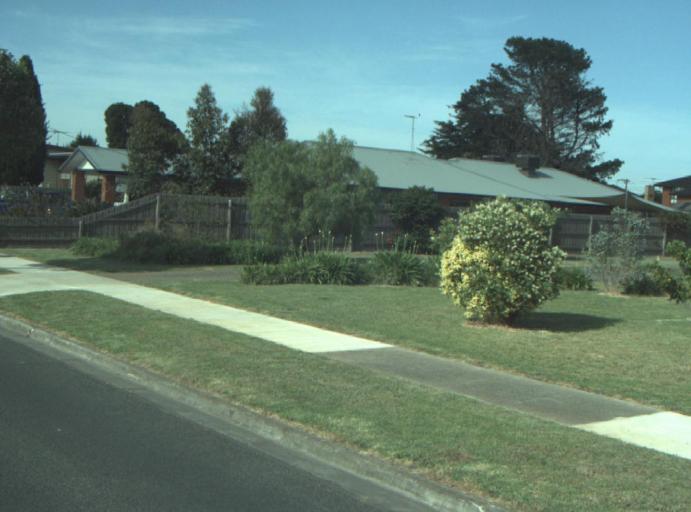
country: AU
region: Victoria
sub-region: Greater Geelong
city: Hamlyn Heights
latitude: -38.1230
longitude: 144.3212
